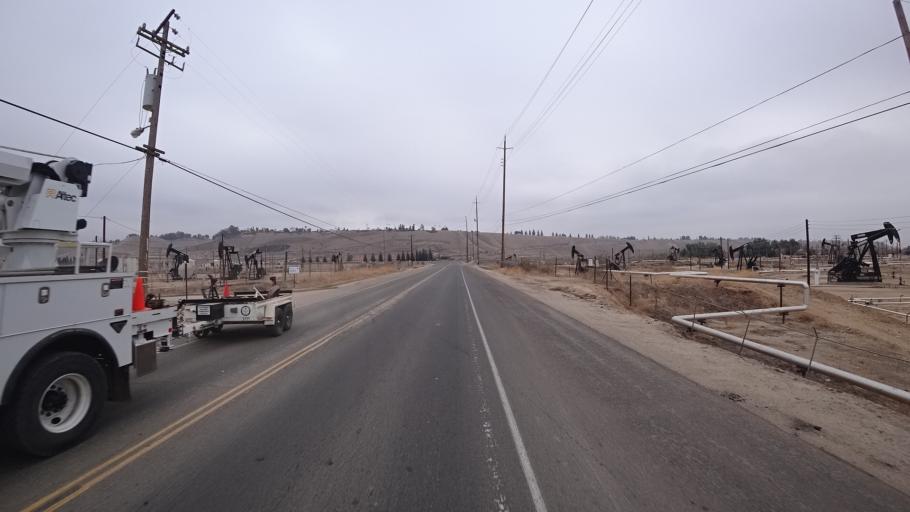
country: US
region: California
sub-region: Kern County
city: Oildale
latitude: 35.4232
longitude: -118.9678
